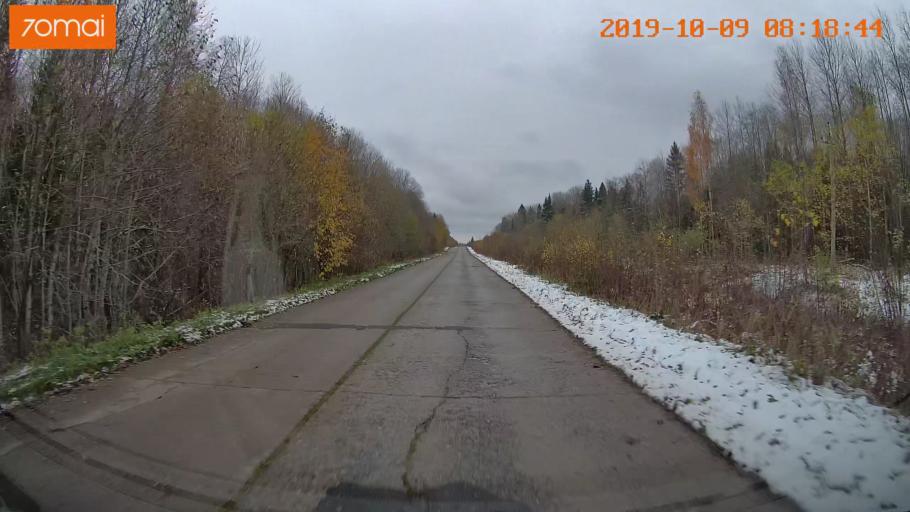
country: RU
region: Vologda
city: Gryazovets
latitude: 58.7408
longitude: 40.2287
